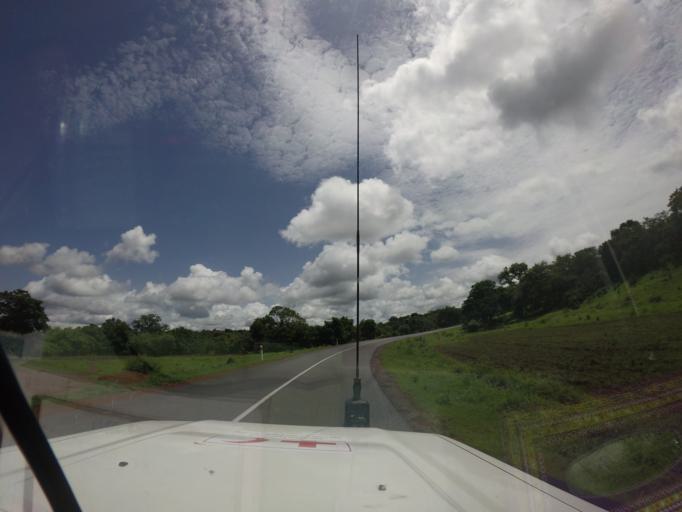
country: SL
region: Northern Province
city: Gberia Fotombu
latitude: 10.0871
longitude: -11.1339
